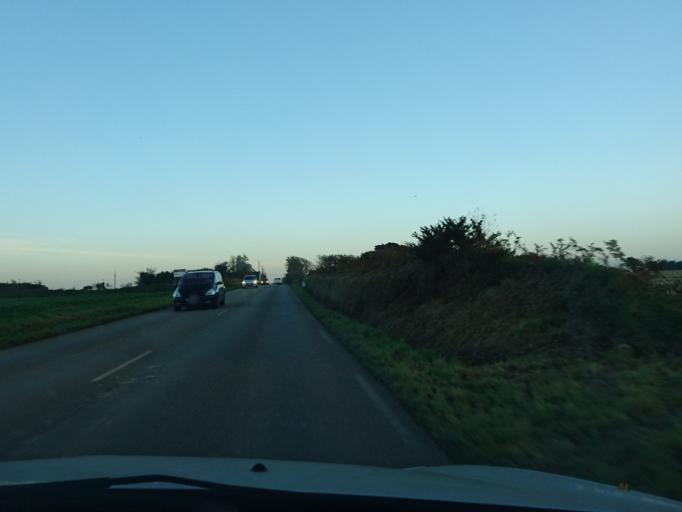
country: FR
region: Brittany
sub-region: Departement du Finistere
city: Lanrivoare
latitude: 48.4627
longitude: -4.6349
